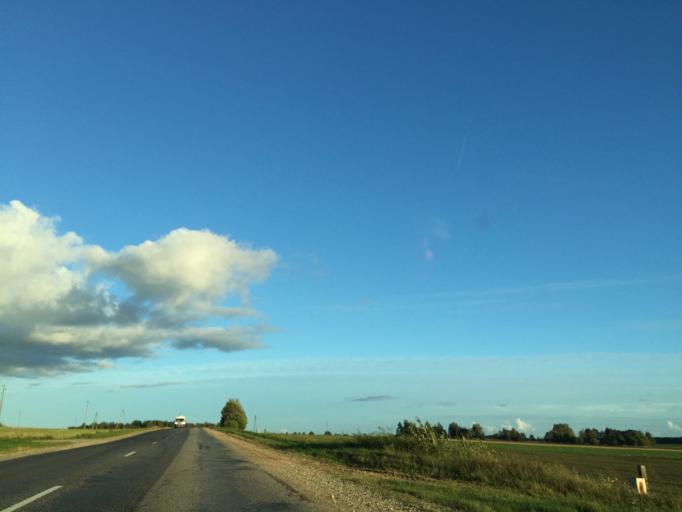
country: LV
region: Saldus Rajons
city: Saldus
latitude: 56.7075
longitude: 22.4212
